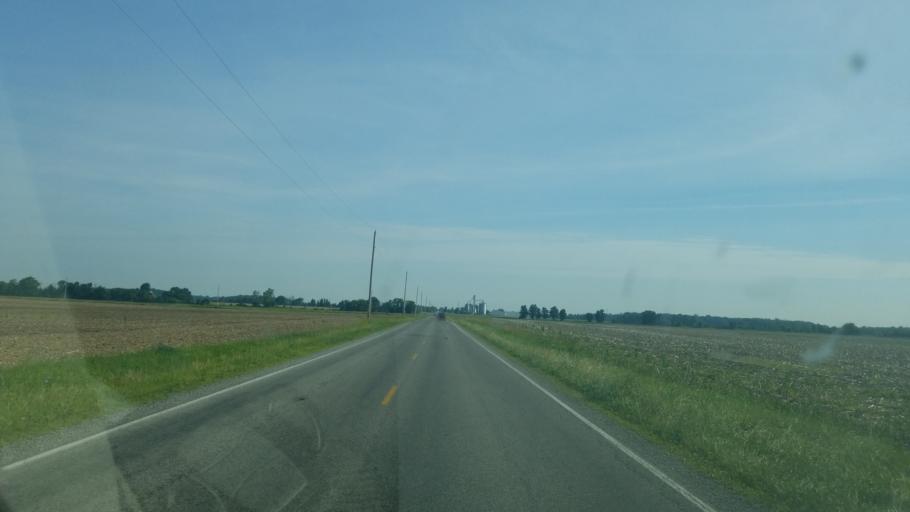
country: US
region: Ohio
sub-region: Hancock County
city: Arlington
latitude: 40.9662
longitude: -83.6985
